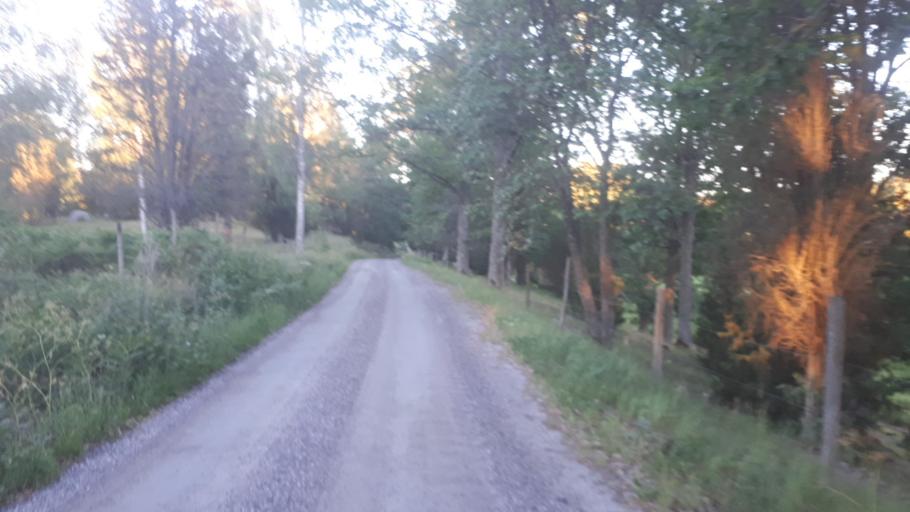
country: SE
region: Soedermanland
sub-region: Flens Kommun
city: Halleforsnas
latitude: 59.0733
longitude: 16.3776
